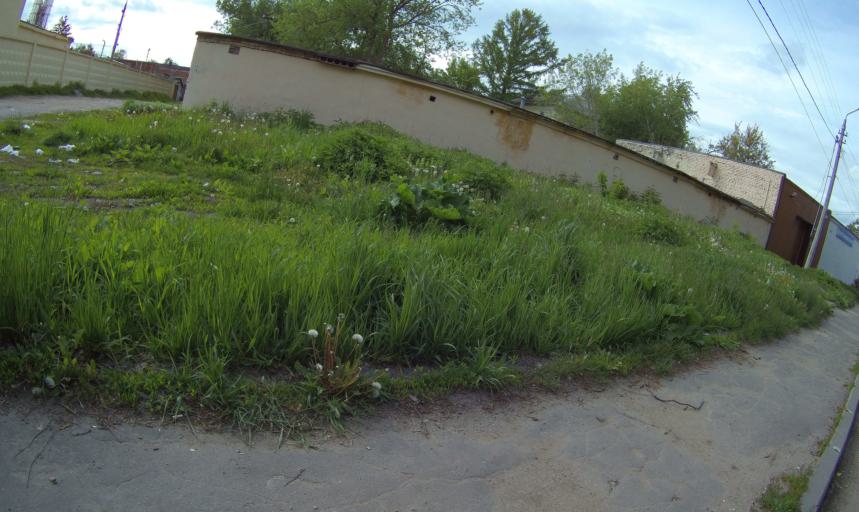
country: RU
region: Moskovskaya
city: Kolomna
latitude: 55.0892
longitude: 38.7703
